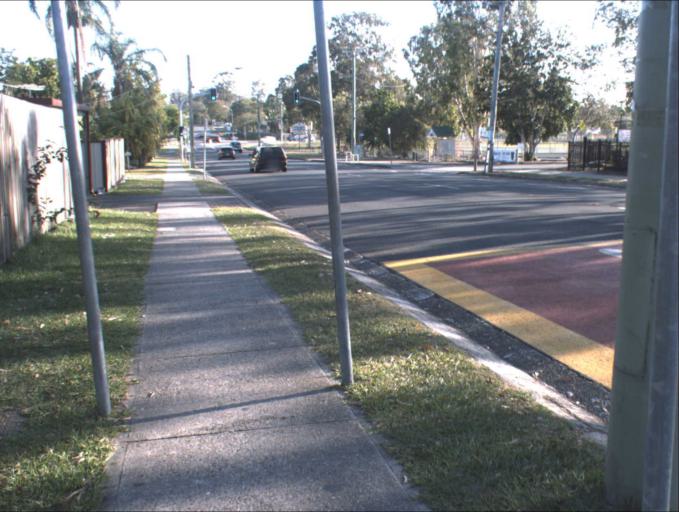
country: AU
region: Queensland
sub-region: Logan
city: Logan City
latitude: -27.6518
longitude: 153.0987
